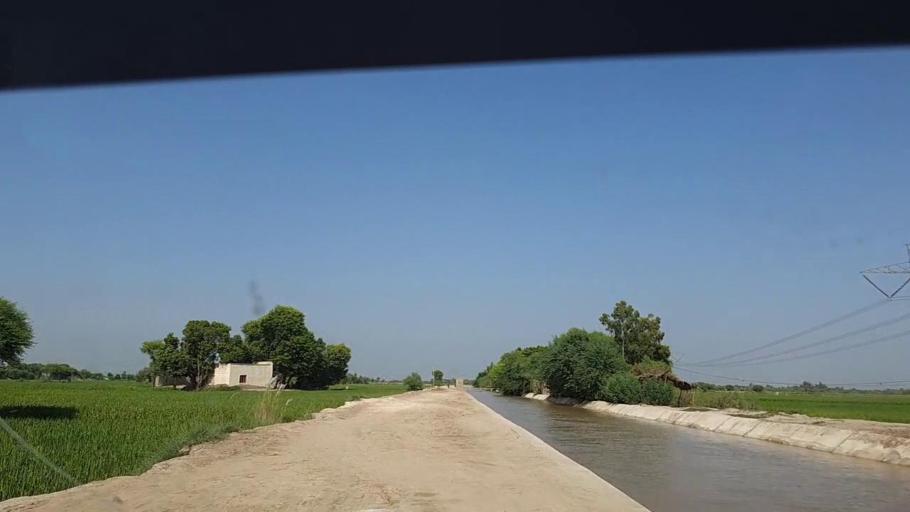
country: PK
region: Sindh
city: Ghauspur
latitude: 28.1575
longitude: 69.0889
